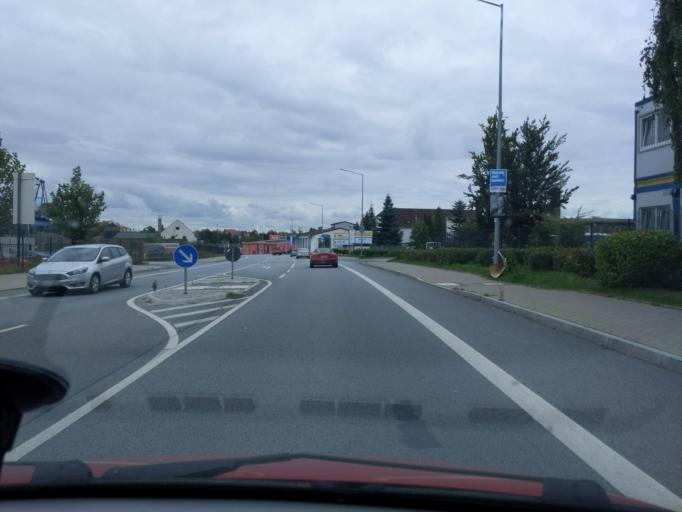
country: DE
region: Saxony
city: Bautzen
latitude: 51.1688
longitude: 14.4289
